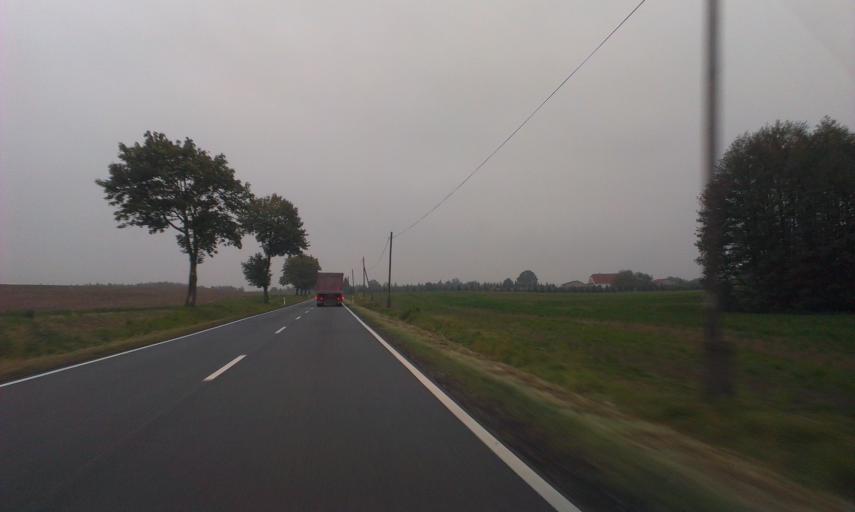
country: PL
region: Kujawsko-Pomorskie
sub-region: Powiat sepolenski
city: Sepolno Krajenskie
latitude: 53.4382
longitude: 17.6136
